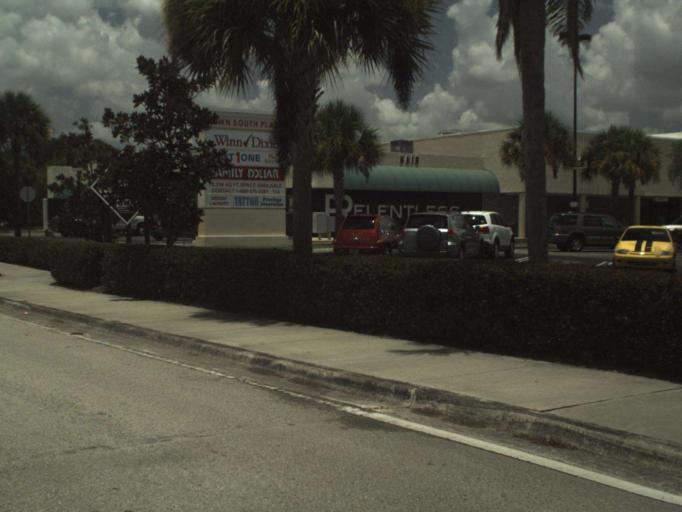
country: US
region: Florida
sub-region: Saint Lucie County
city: White City
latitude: 27.3743
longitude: -80.3278
